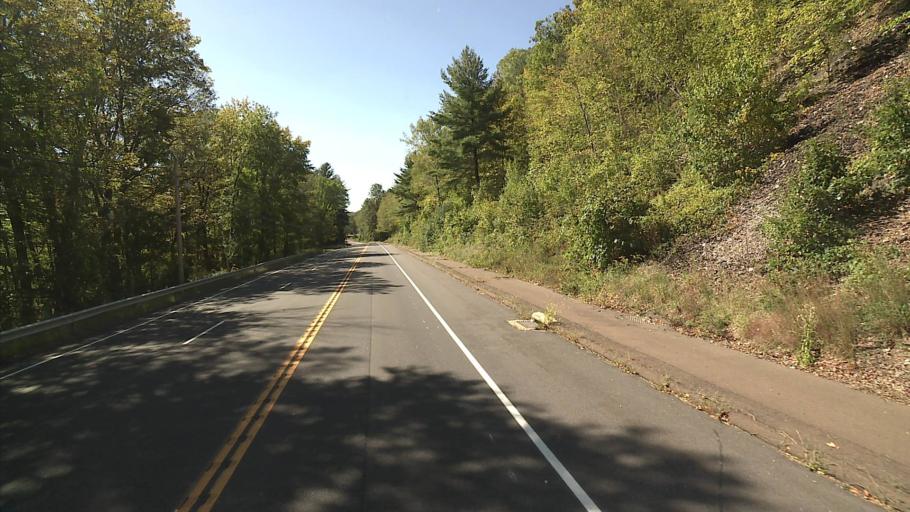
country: US
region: Connecticut
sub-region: New Haven County
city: Woodbridge
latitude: 41.3863
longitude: -72.9733
